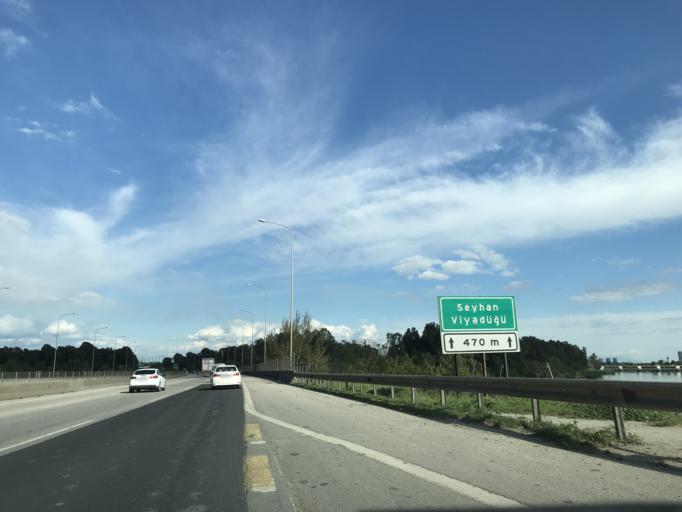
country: TR
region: Adana
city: Adana
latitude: 37.0247
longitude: 35.3223
